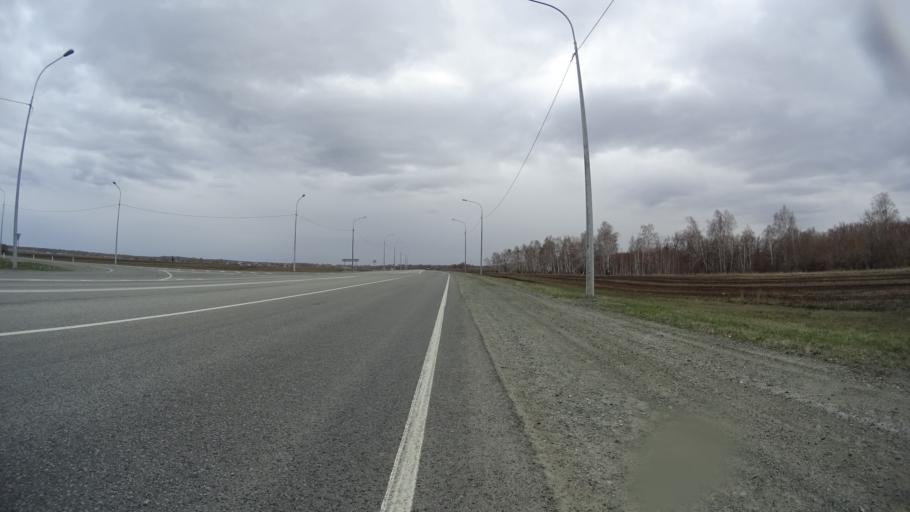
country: RU
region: Chelyabinsk
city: Krasnogorskiy
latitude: 54.6835
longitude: 61.2472
